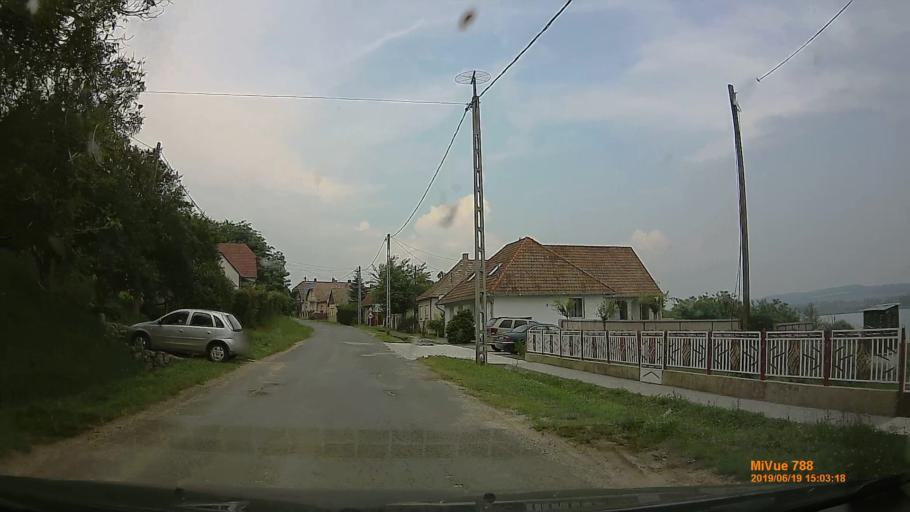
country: HU
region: Baranya
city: Szigetvar
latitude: 46.0937
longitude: 17.8057
